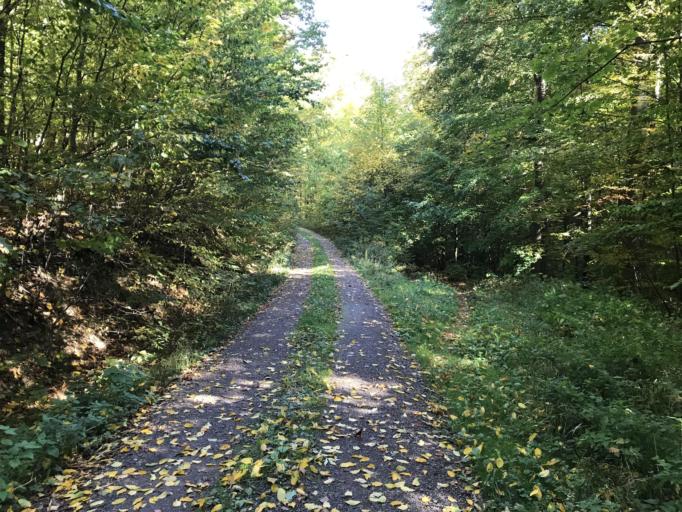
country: DE
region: Saxony-Anhalt
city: Wippra
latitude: 51.6310
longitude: 11.2266
